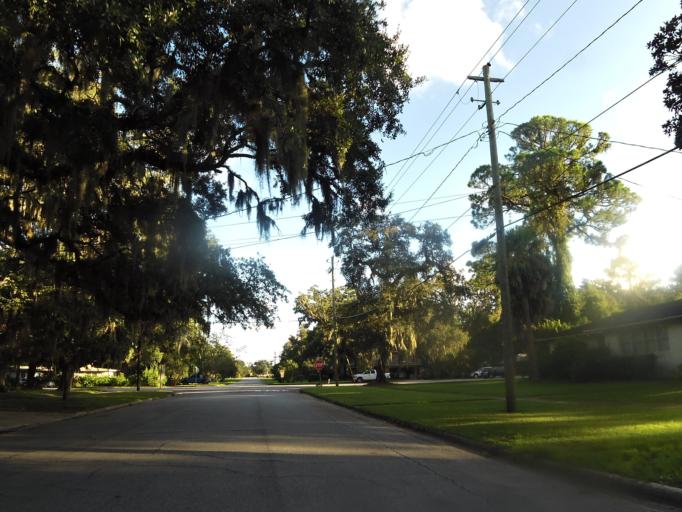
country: US
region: Georgia
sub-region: Glynn County
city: Brunswick
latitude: 31.1337
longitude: -81.4876
